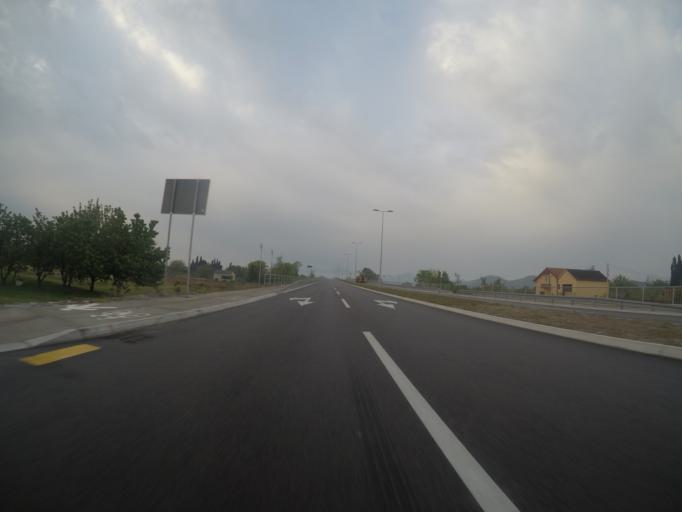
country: ME
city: Mojanovici
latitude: 42.3511
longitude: 19.2226
